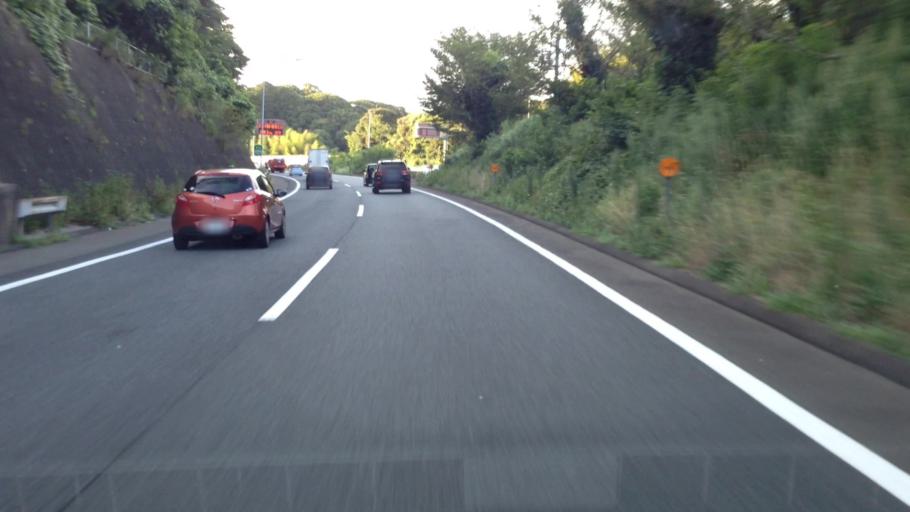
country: JP
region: Kanagawa
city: Kamakura
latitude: 35.3631
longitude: 139.5985
